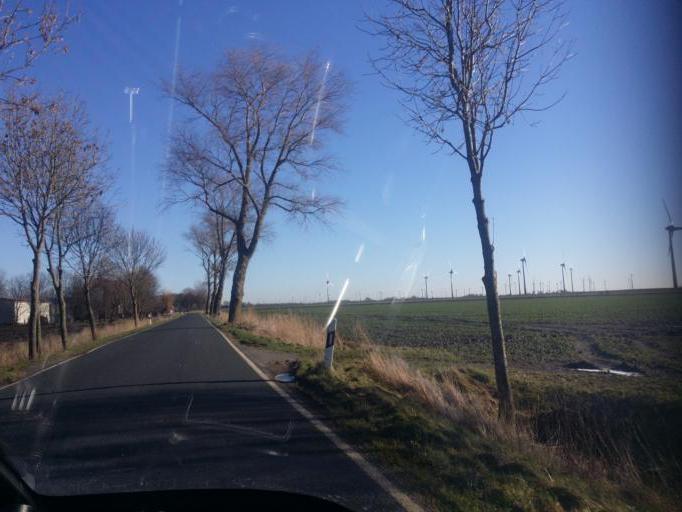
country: DE
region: Schleswig-Holstein
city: Strubbel
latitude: 54.2739
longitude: 8.9526
